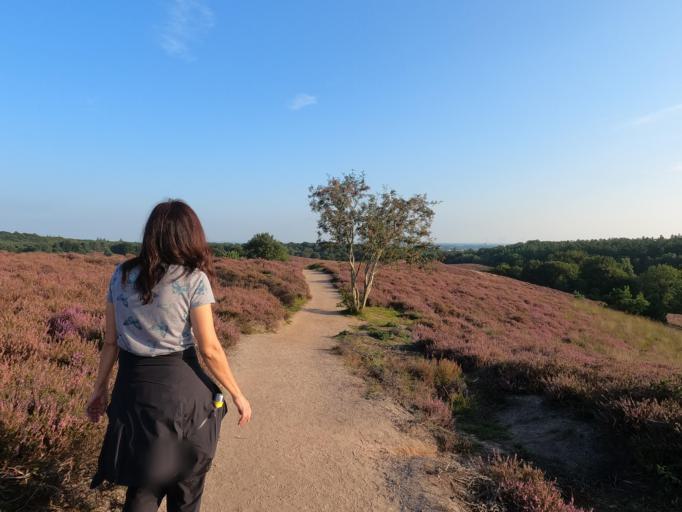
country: NL
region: Gelderland
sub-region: Gemeente Rheden
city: Rheden
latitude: 52.0264
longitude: 6.0263
